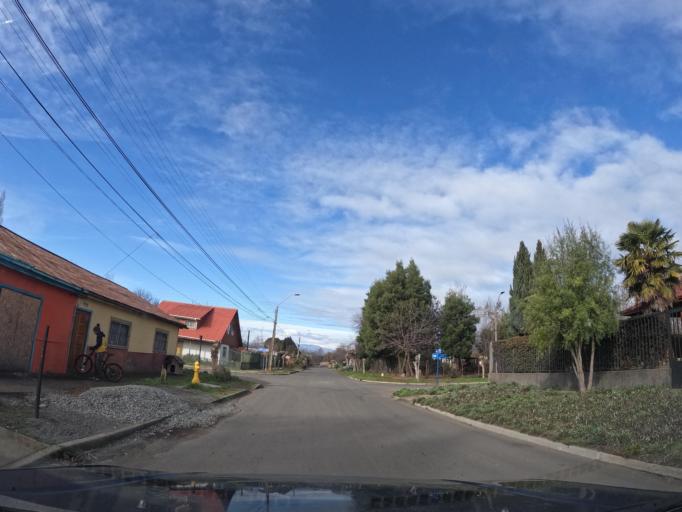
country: CL
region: Biobio
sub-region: Provincia de Nuble
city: Coihueco
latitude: -36.7039
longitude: -71.8883
